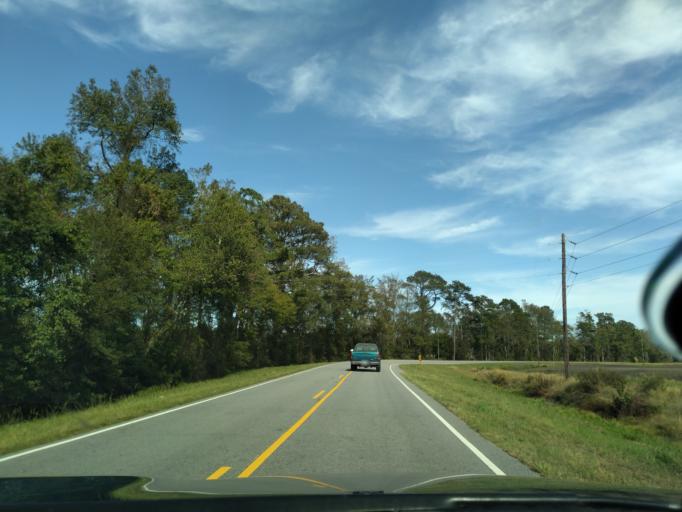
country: US
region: North Carolina
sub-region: Beaufort County
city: Belhaven
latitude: 35.6256
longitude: -76.6301
